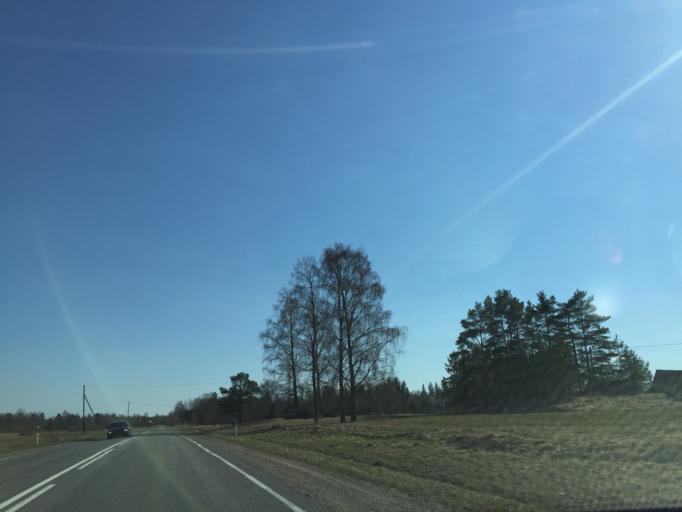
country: EE
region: Viljandimaa
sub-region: Viiratsi vald
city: Viiratsi
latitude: 58.2731
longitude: 25.6965
